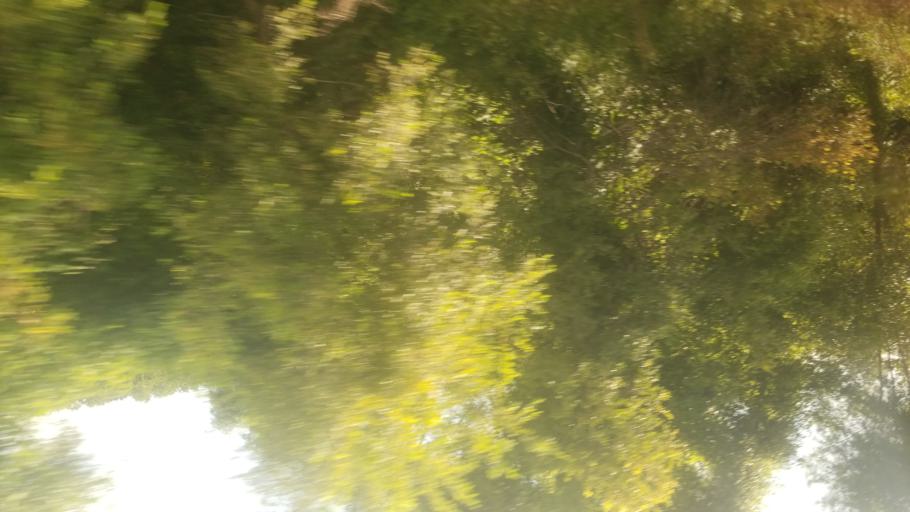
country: US
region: Kansas
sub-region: Wyandotte County
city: Edwardsville
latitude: 39.0502
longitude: -94.8438
